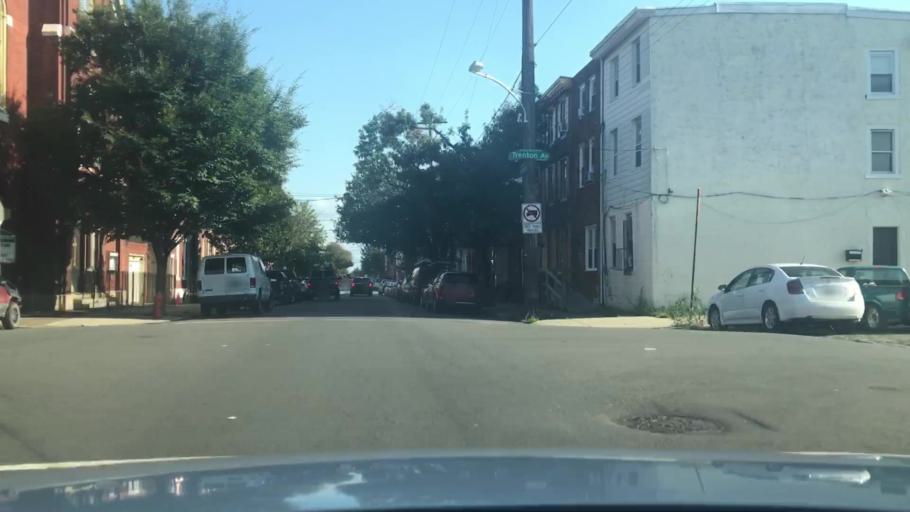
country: US
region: Pennsylvania
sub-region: Philadelphia County
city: Philadelphia
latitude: 39.9825
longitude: -75.1251
